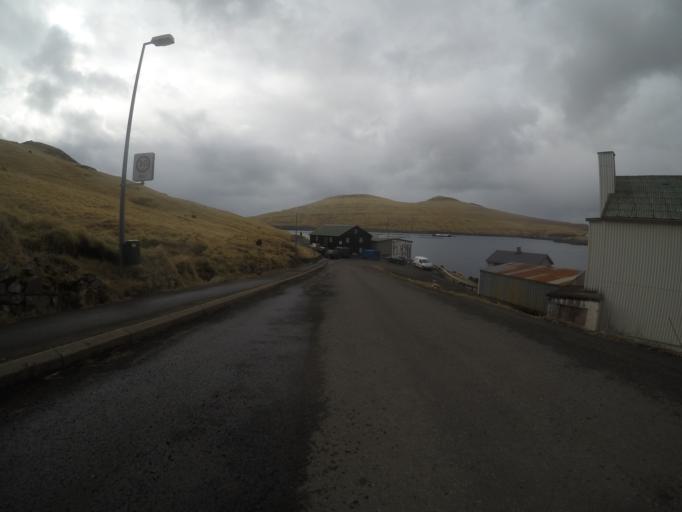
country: FO
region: Vagar
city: Midvagur
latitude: 62.0502
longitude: -7.1499
